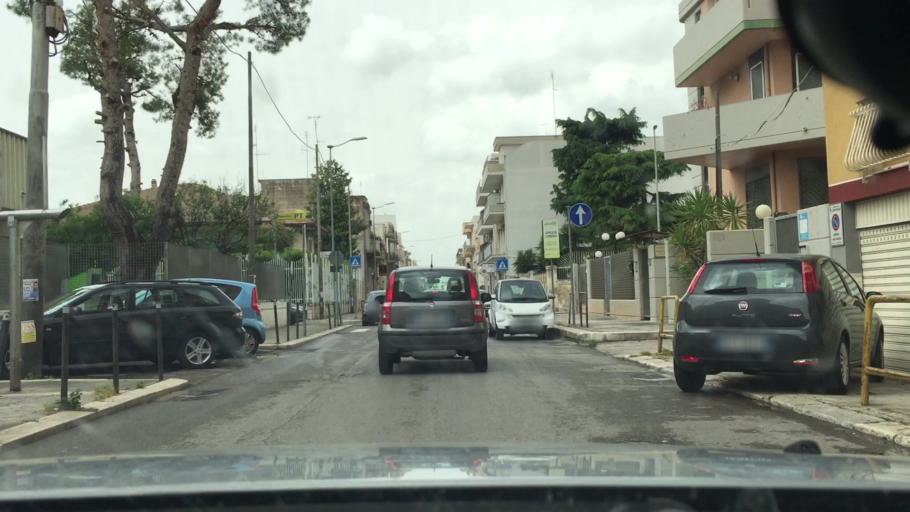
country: IT
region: Apulia
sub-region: Provincia di Bari
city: Capurso
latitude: 41.0481
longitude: 16.9250
